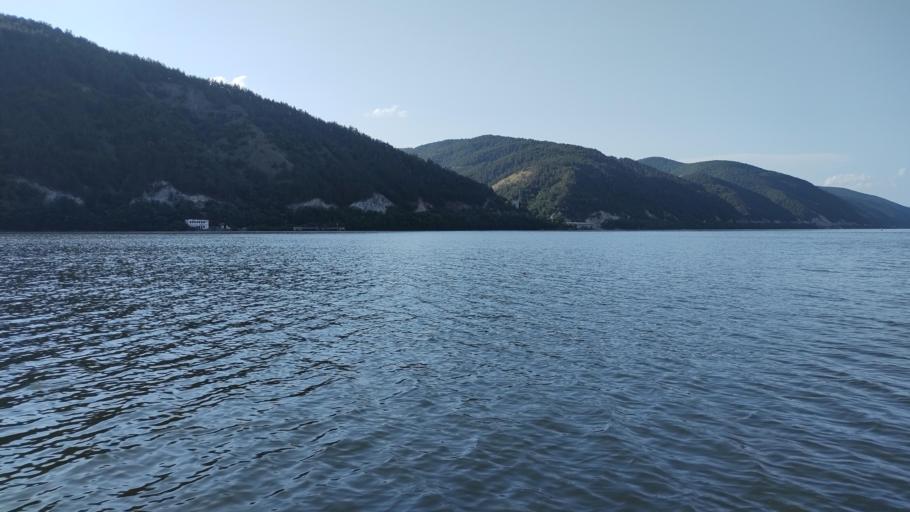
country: RO
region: Mehedinti
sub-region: Comuna Svinita
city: Svinita
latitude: 44.5208
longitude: 22.2052
